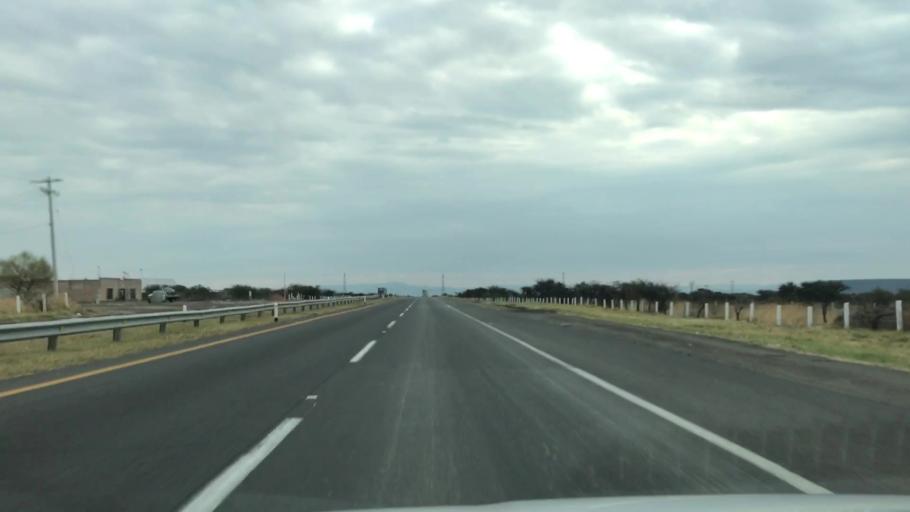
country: MX
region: Jalisco
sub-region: Lagos de Moreno
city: Cristeros [Fraccionamiento]
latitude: 21.3048
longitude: -102.0919
